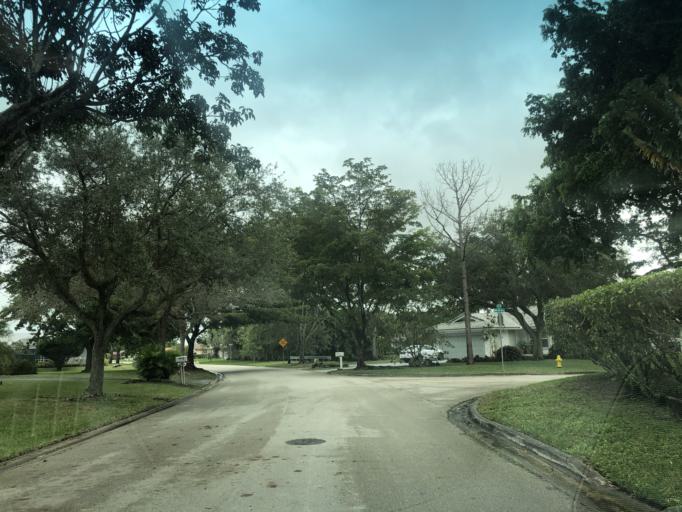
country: US
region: Florida
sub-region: Broward County
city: Coral Springs
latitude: 26.2550
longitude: -80.2416
